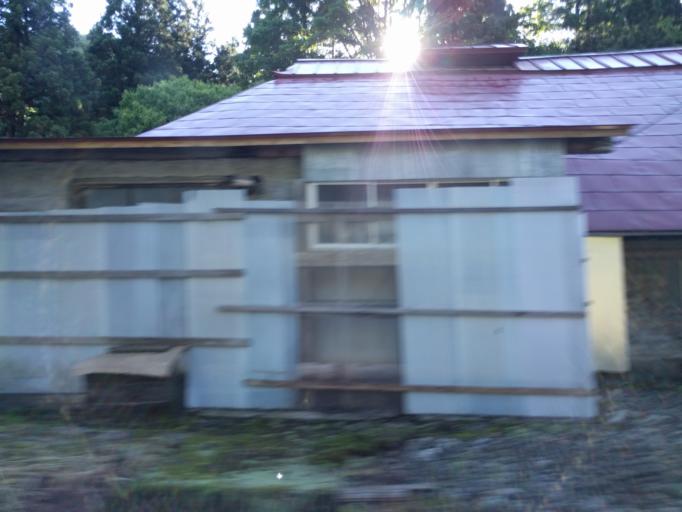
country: JP
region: Fukushima
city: Kitakata
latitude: 37.3643
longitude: 139.8109
